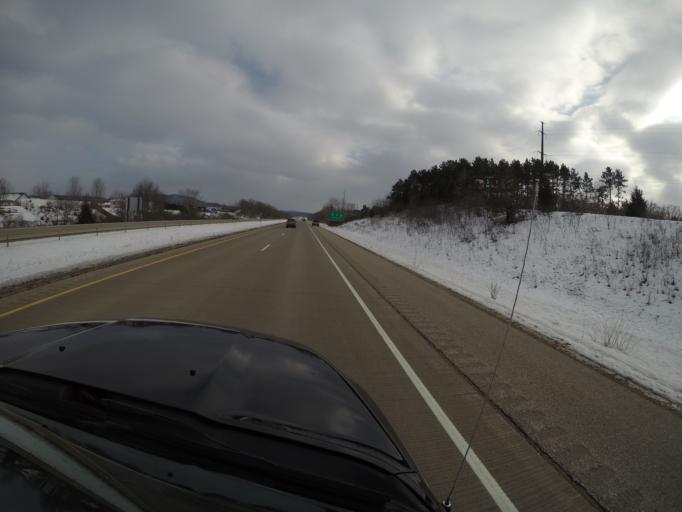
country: US
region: Wisconsin
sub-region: La Crosse County
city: Holmen
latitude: 43.9528
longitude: -91.2763
